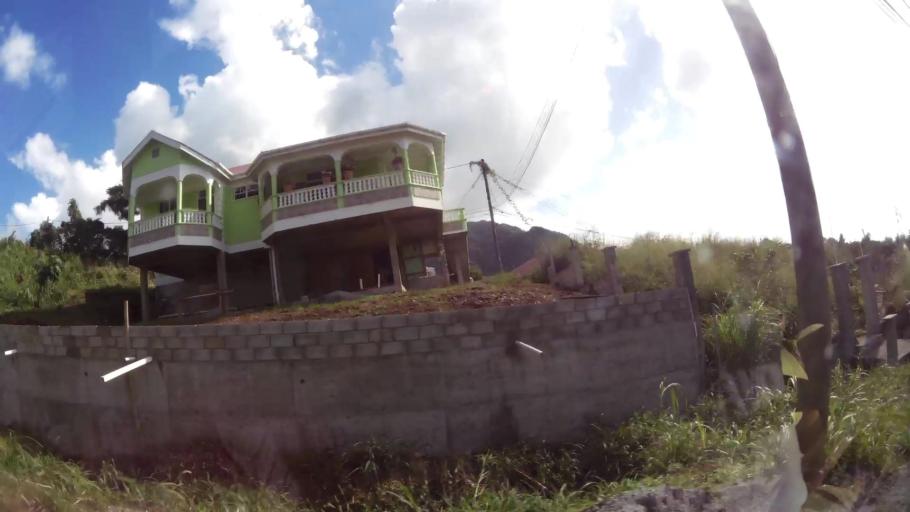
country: DM
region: Saint George
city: Roseau
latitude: 15.2838
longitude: -61.3729
